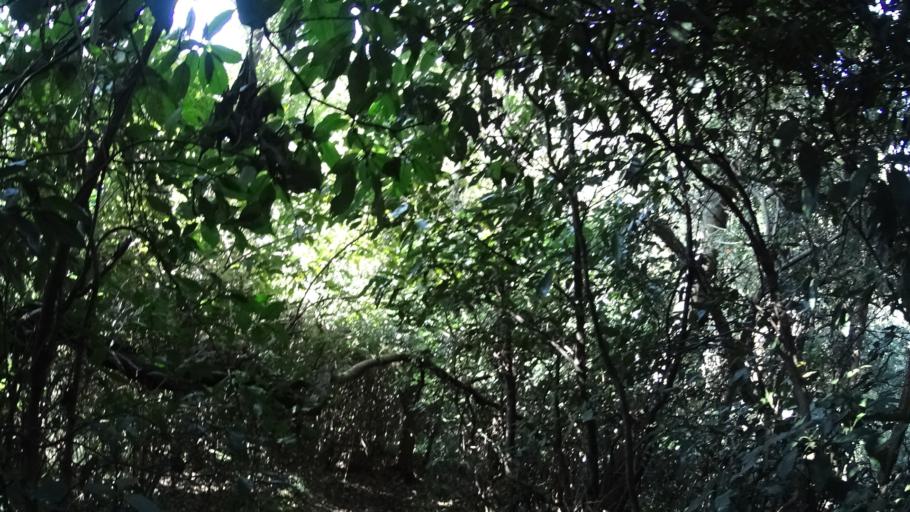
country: JP
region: Kanagawa
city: Hayama
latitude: 35.2775
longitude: 139.6130
